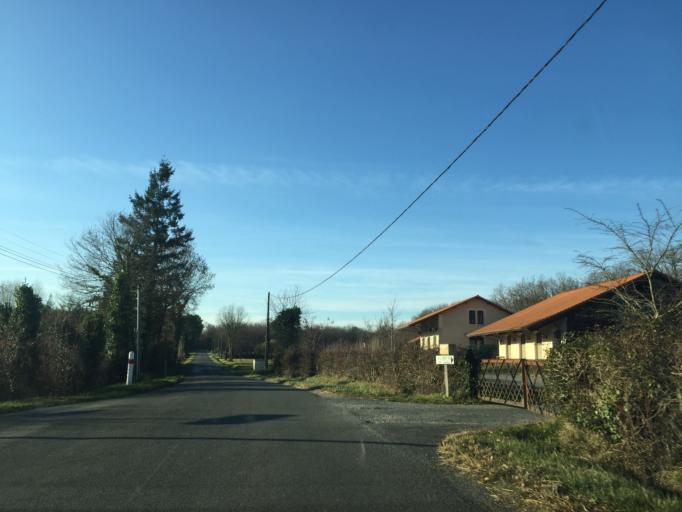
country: FR
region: Aquitaine
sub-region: Departement de la Dordogne
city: Riberac
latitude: 45.2022
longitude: 0.3603
